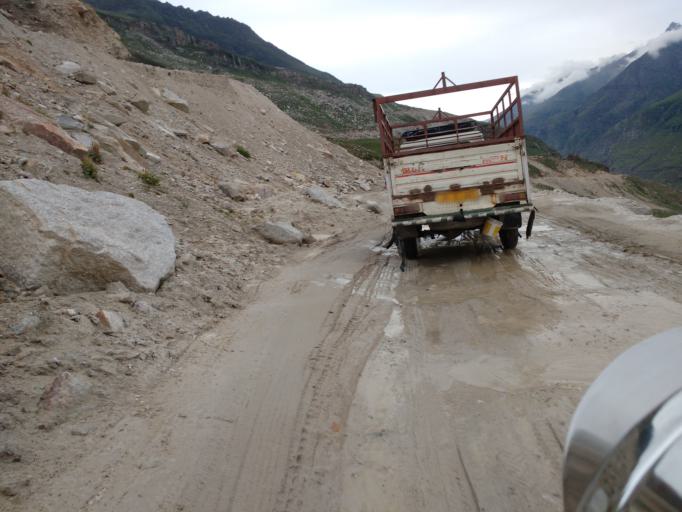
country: IN
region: Himachal Pradesh
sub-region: Kulu
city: Manali
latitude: 32.3782
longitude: 77.2687
